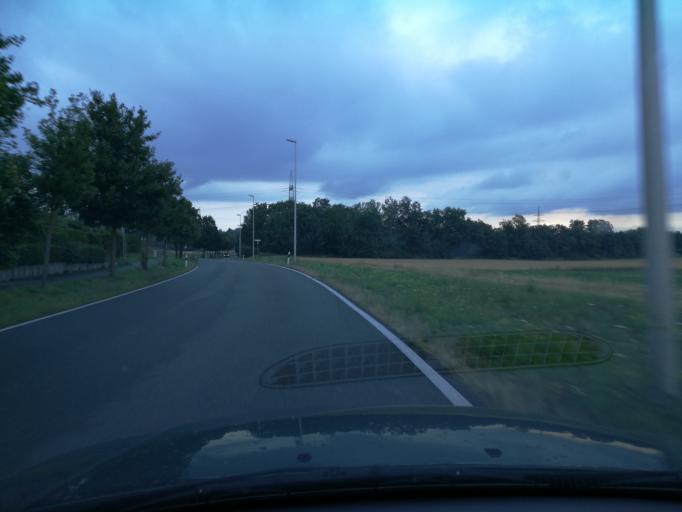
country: DE
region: Bavaria
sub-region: Regierungsbezirk Mittelfranken
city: Erlangen
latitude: 49.5567
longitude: 10.9611
